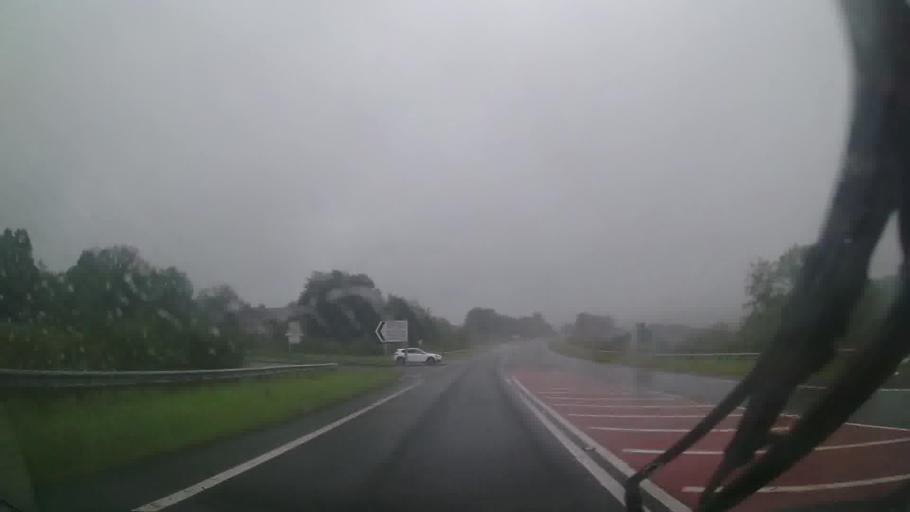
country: GB
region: Wales
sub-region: Carmarthenshire
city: Whitland
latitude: 51.7741
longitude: -4.6120
